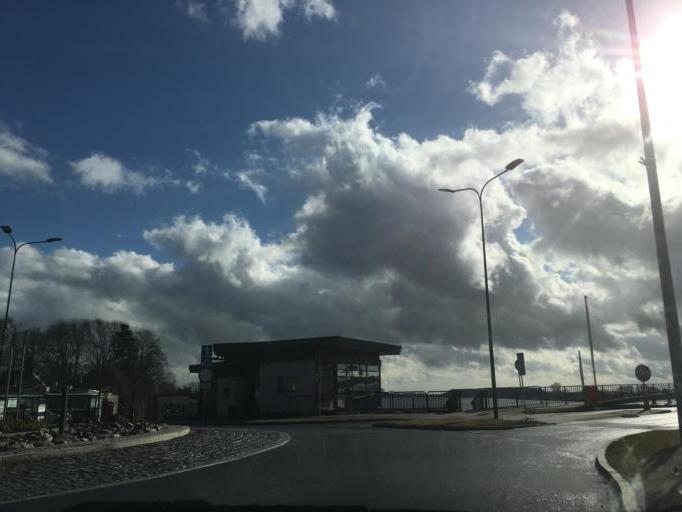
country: PL
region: Pomeranian Voivodeship
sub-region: Powiat gdanski
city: Cedry Wielkie
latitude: 54.3438
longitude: 18.8254
